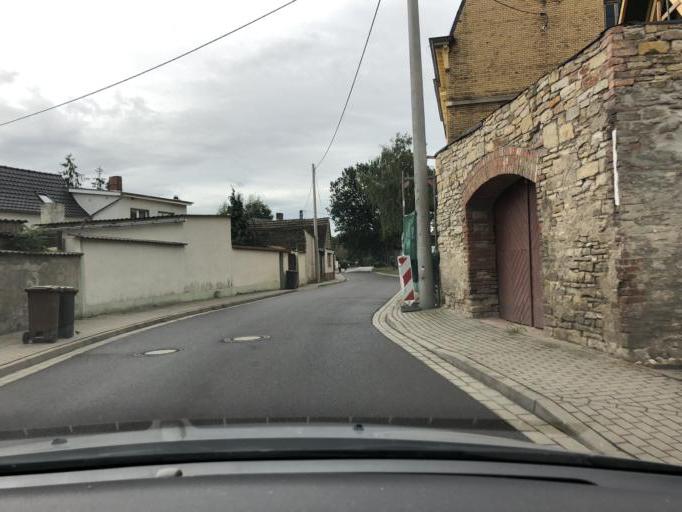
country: DE
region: Saxony-Anhalt
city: Calbe
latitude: 51.8751
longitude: 11.7776
